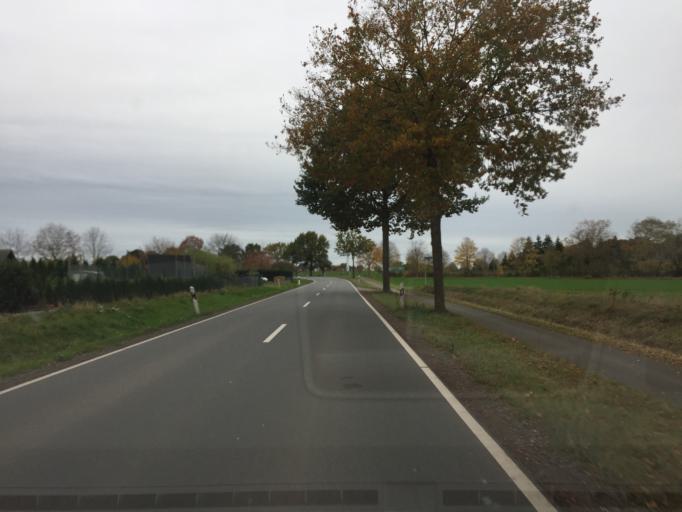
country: DE
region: Lower Saxony
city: Linsburg
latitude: 52.5916
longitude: 9.2975
